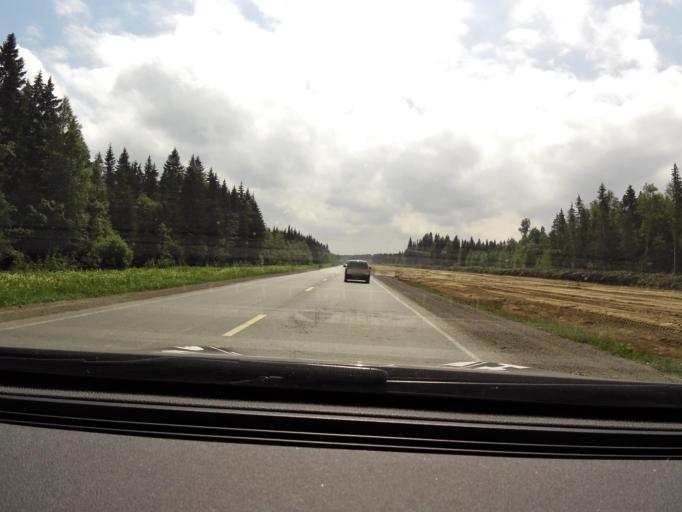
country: RU
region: Perm
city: Kukushtan
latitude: 57.6565
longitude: 56.4417
